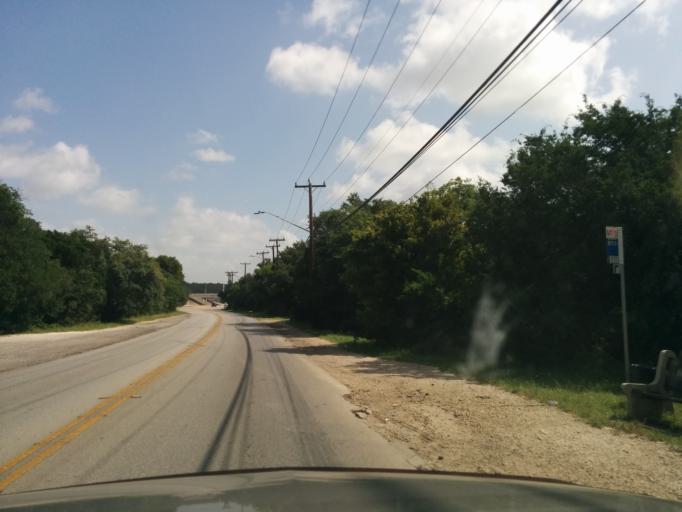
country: US
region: Texas
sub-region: Bexar County
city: Helotes
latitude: 29.5833
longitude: -98.6315
